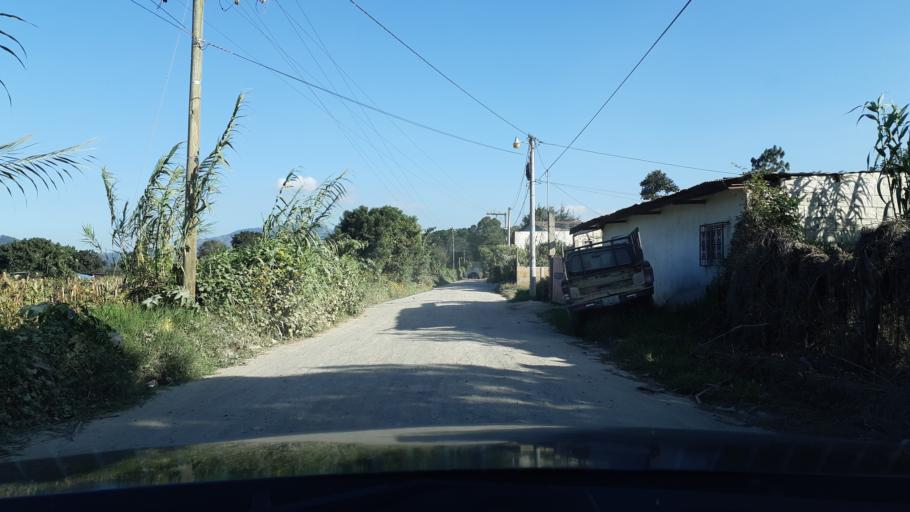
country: GT
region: Chimaltenango
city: El Tejar
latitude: 14.6377
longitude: -90.8023
